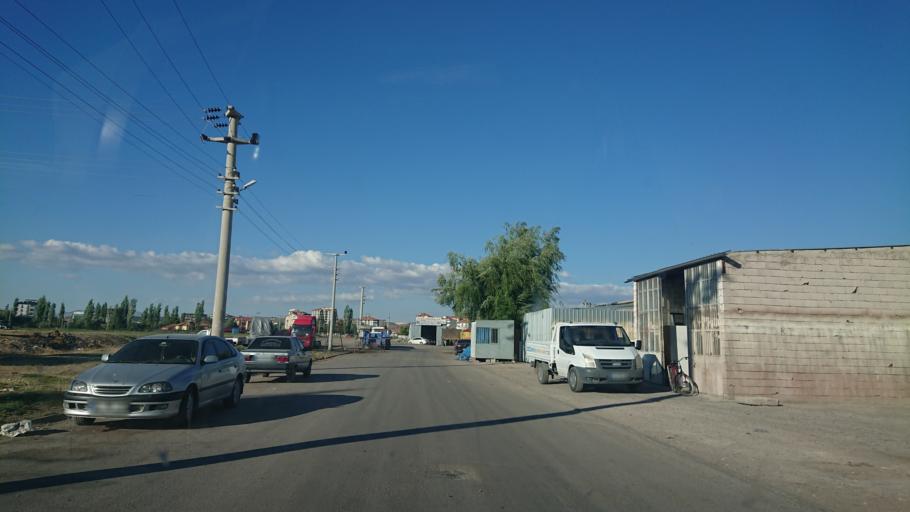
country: TR
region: Aksaray
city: Aksaray
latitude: 38.3772
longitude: 33.9891
